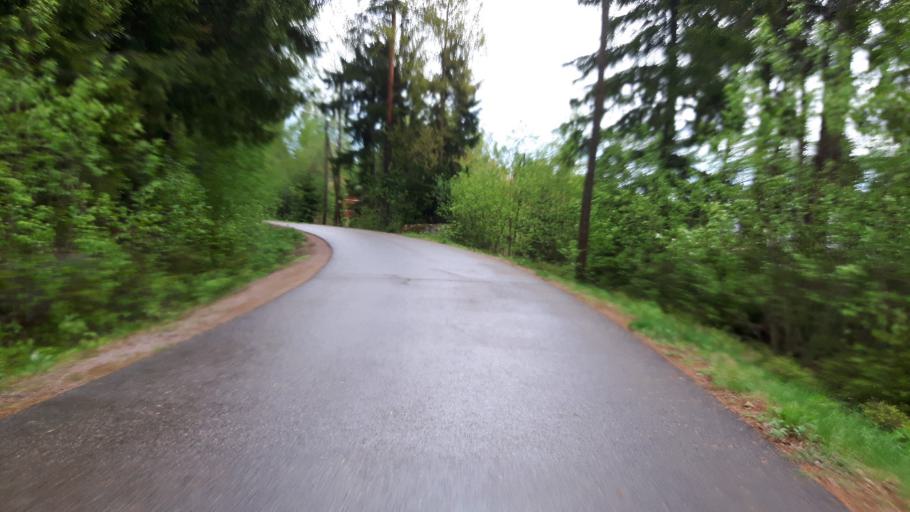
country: FI
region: Kymenlaakso
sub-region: Kotka-Hamina
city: Karhula
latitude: 60.5596
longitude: 27.0259
